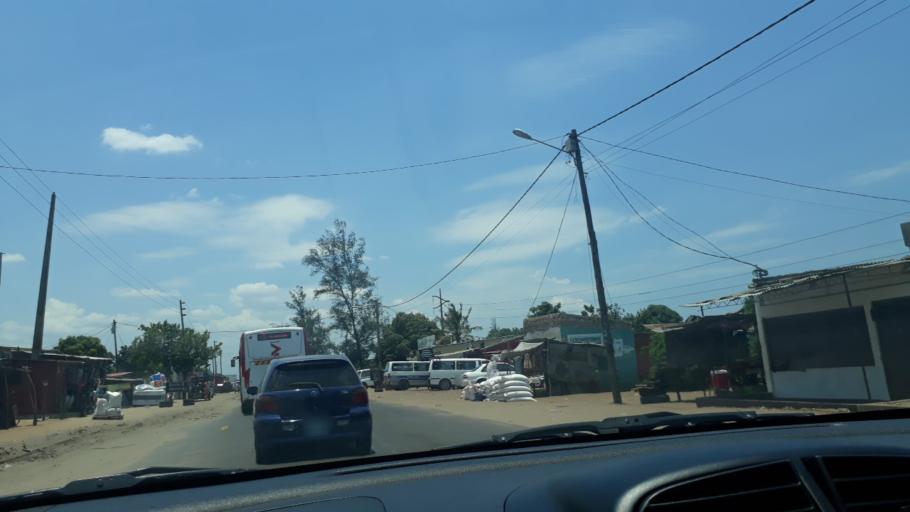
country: MZ
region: Maputo City
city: Maputo
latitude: -25.8910
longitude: 32.6028
